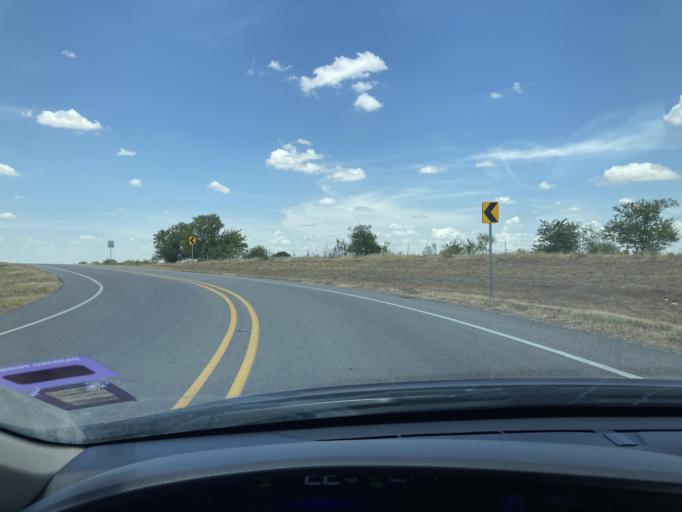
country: US
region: Texas
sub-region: Navarro County
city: Corsicana
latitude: 32.0482
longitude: -96.4909
